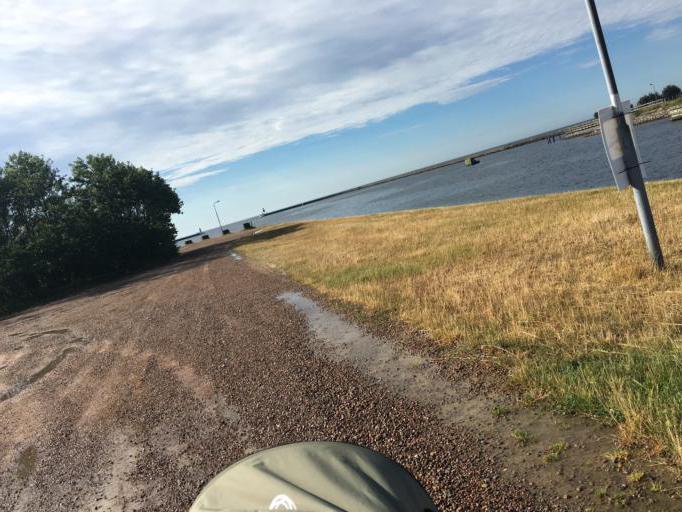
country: SE
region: Skane
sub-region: Vellinge Kommun
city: Hollviken
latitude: 55.3990
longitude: 12.9449
